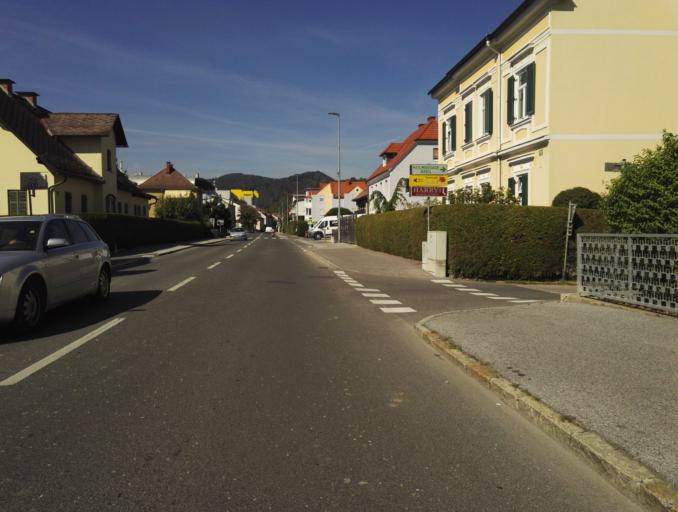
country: AT
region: Styria
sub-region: Politischer Bezirk Graz-Umgebung
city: Gratkorn
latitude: 47.1304
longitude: 15.3423
